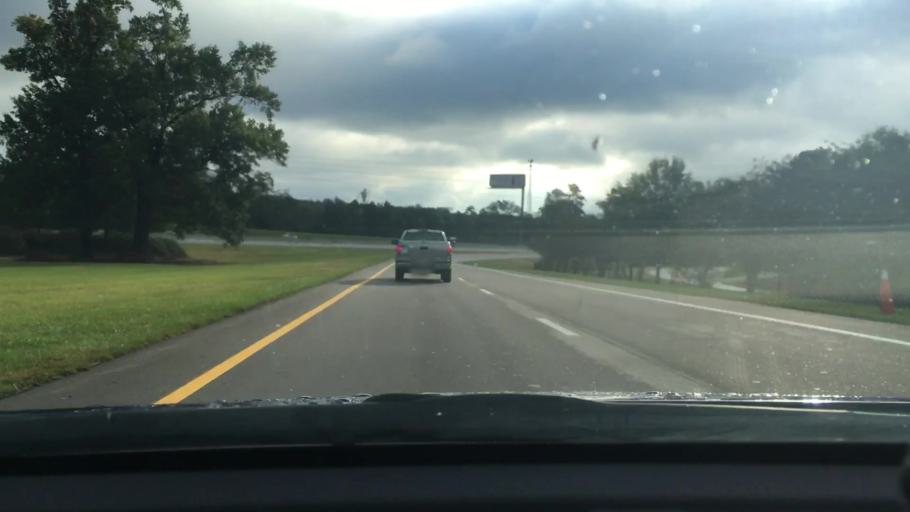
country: US
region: South Carolina
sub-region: Lexington County
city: Irmo
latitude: 34.0975
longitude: -81.1753
